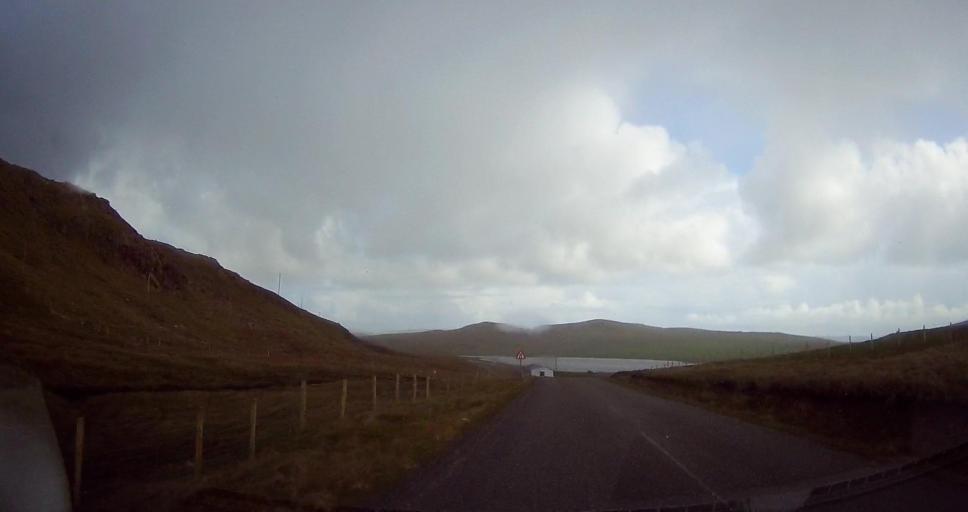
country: GB
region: Scotland
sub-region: Shetland Islands
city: Lerwick
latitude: 60.5440
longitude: -1.3432
